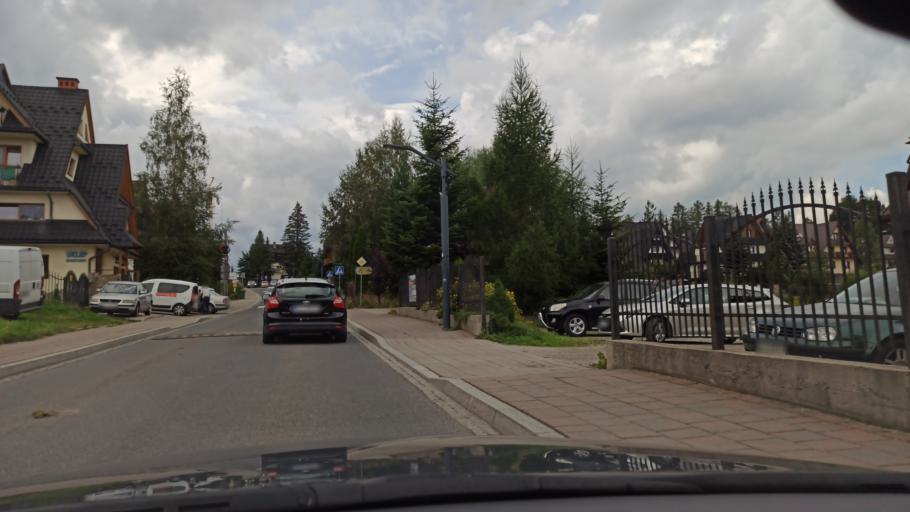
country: PL
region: Lesser Poland Voivodeship
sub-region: Powiat tatrzanski
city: Zakopane
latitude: 49.2910
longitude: 19.9797
